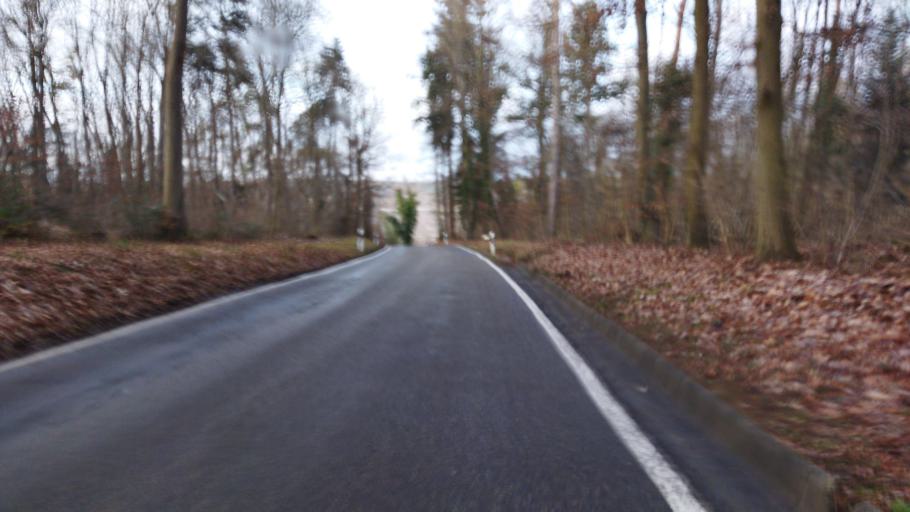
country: DE
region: Baden-Wuerttemberg
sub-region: Regierungsbezirk Stuttgart
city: Mundelsheim
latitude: 48.9925
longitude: 9.1992
